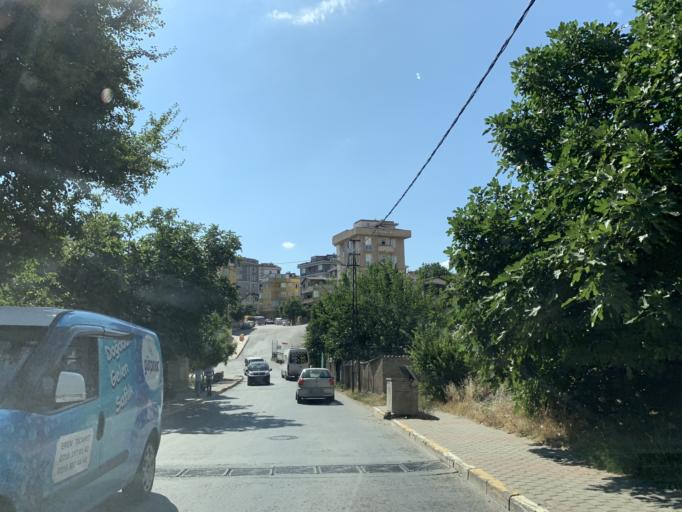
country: TR
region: Istanbul
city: Pendik
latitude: 40.8888
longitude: 29.2757
